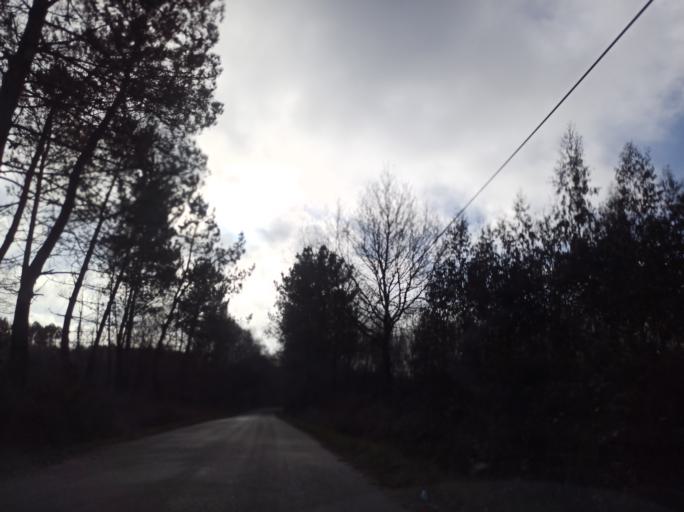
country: ES
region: Galicia
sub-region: Provincia da Coruna
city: Sobrado
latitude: 43.0954
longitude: -7.9753
